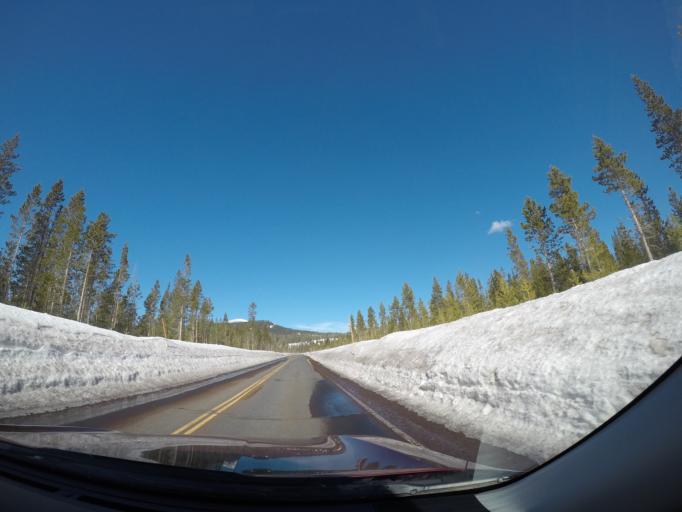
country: US
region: Oregon
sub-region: Deschutes County
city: Sunriver
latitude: 43.9778
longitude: -121.6109
